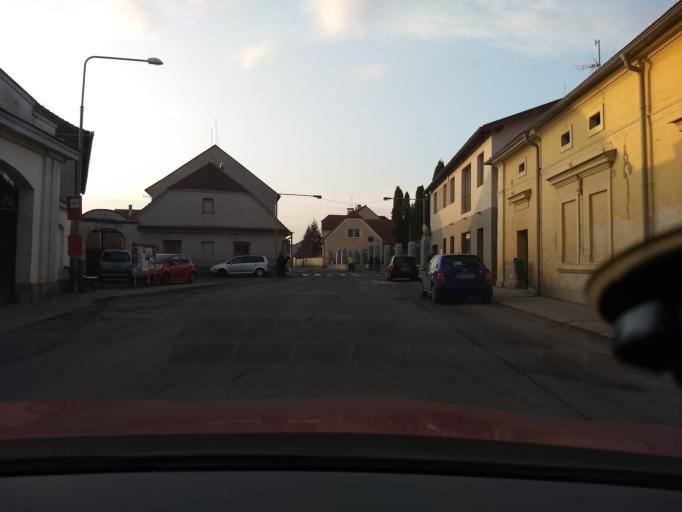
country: CZ
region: Central Bohemia
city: Rudna
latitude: 50.0419
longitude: 14.1865
